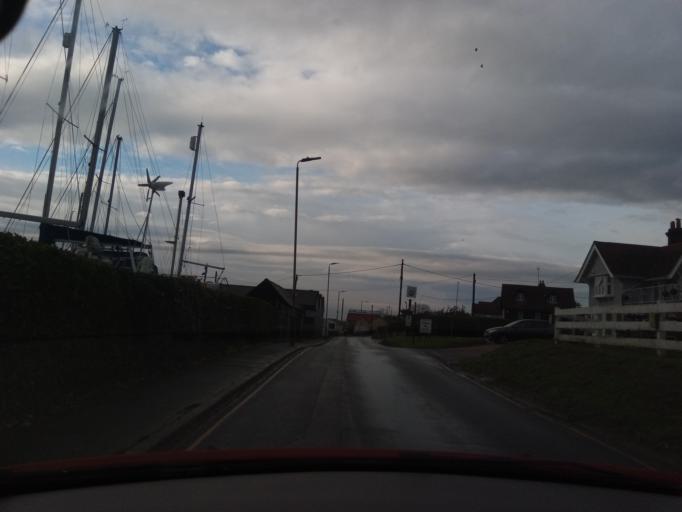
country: GB
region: England
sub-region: Essex
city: West Mersea
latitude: 51.7764
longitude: 0.9011
